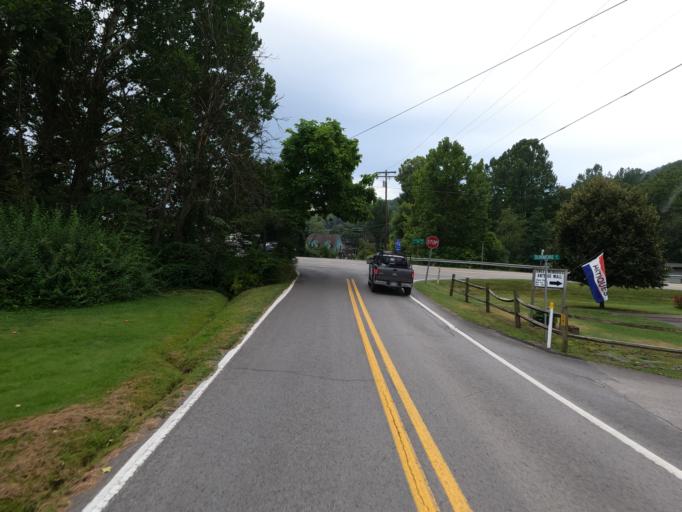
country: US
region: West Virginia
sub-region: Marion County
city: Fairmont
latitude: 39.4963
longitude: -80.0929
